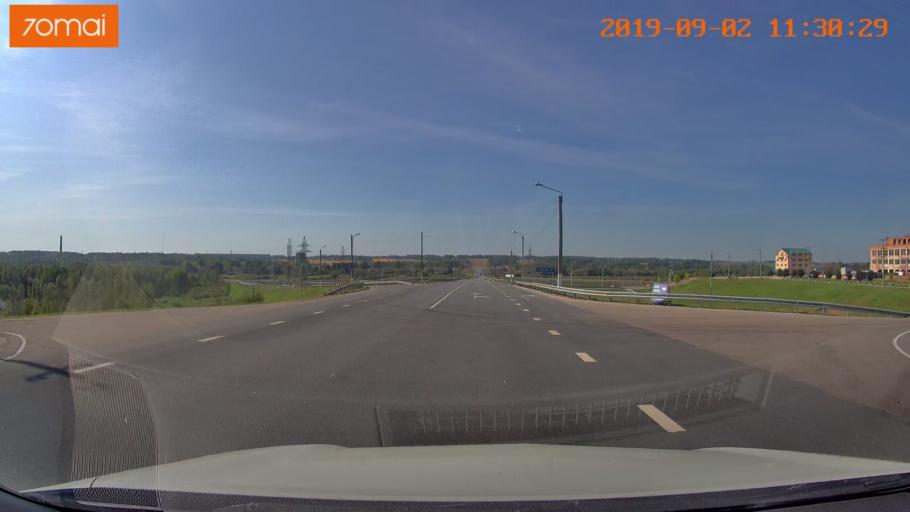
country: RU
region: Smolensk
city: Roslavl'
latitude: 53.9836
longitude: 32.8330
